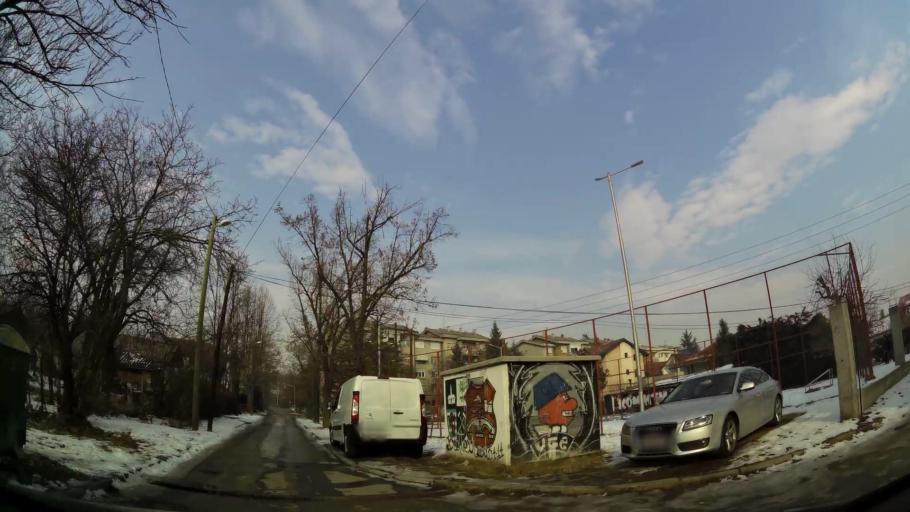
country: MK
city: Creshevo
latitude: 42.0023
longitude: 21.4920
